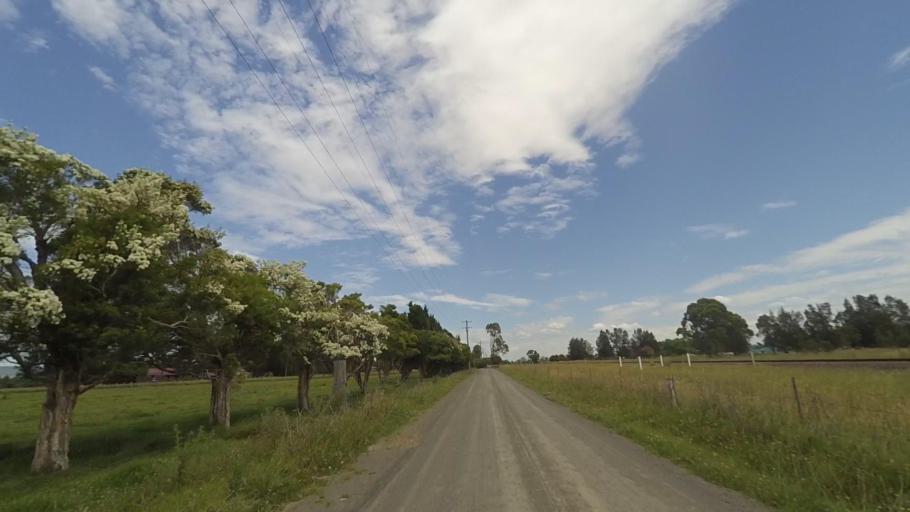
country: AU
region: New South Wales
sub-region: Shoalhaven Shire
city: Berry
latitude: -34.7931
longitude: 150.6775
